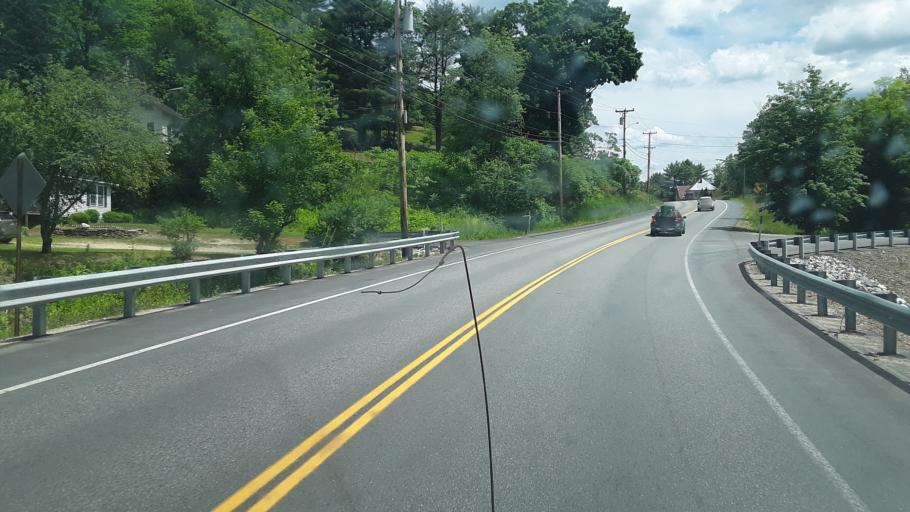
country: US
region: Maine
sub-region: Oxford County
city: Dixfield
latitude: 44.5302
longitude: -70.4485
